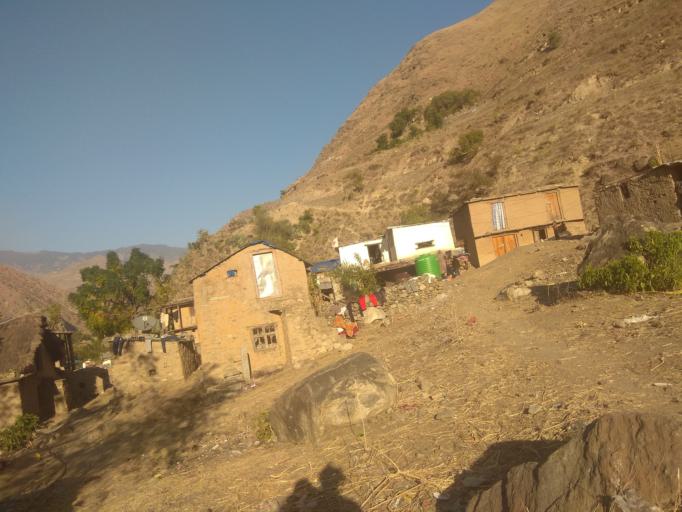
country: NP
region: Mid Western
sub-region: Bheri Zone
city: Dailekh
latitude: 29.2762
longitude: 81.7296
